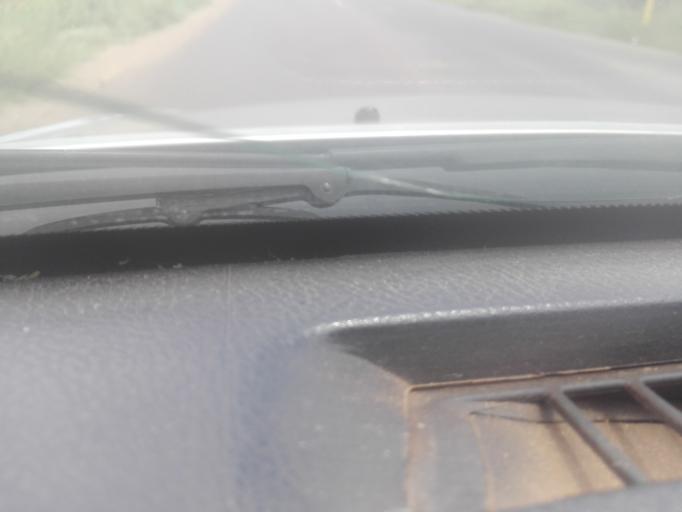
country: BW
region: South East
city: Gaborone
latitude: -24.6230
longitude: 25.9369
